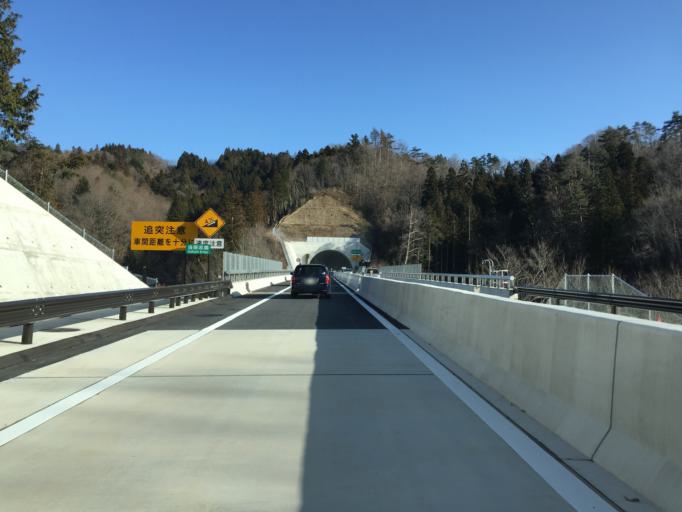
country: JP
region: Fukushima
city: Hobaramachi
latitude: 37.7557
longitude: 140.6207
